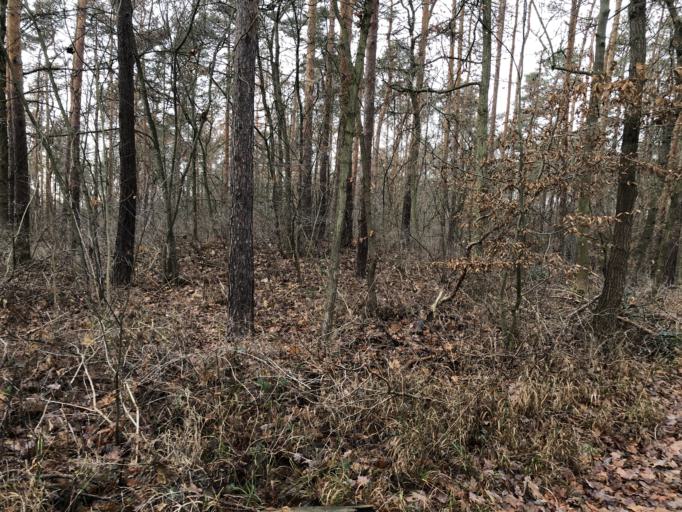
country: DE
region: Saxony-Anhalt
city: Halle Neustadt
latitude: 51.4980
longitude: 11.8990
